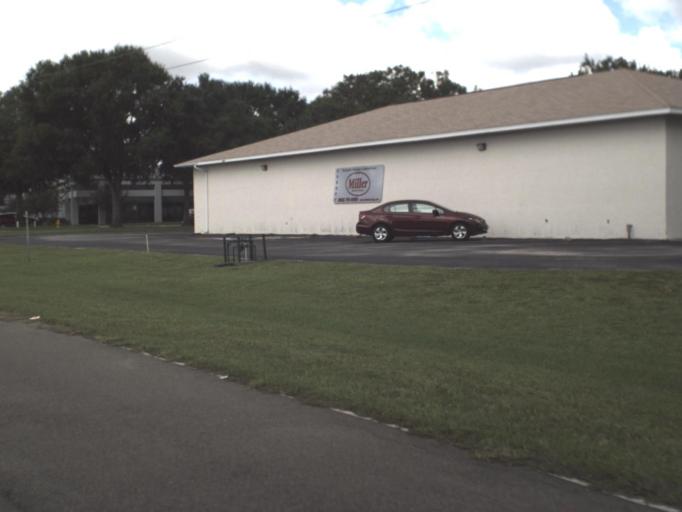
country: US
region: Florida
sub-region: Polk County
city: Medulla
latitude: 27.9967
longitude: -81.9957
